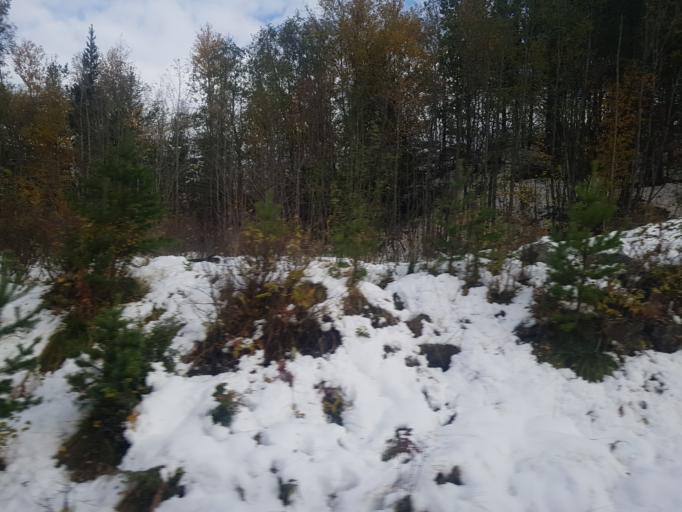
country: NO
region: Oppland
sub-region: Dovre
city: Dombas
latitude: 62.0875
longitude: 9.1235
